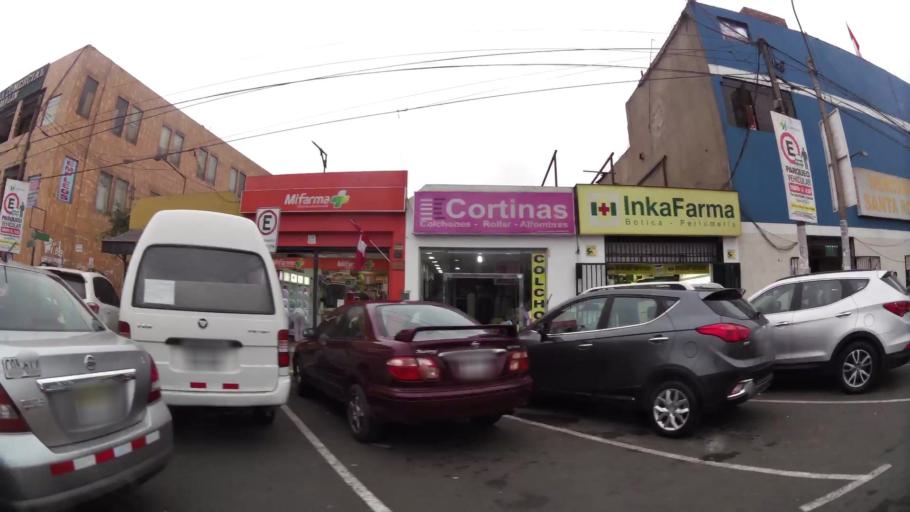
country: PE
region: Lima
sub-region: Lima
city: La Molina
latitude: -12.0693
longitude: -76.9579
